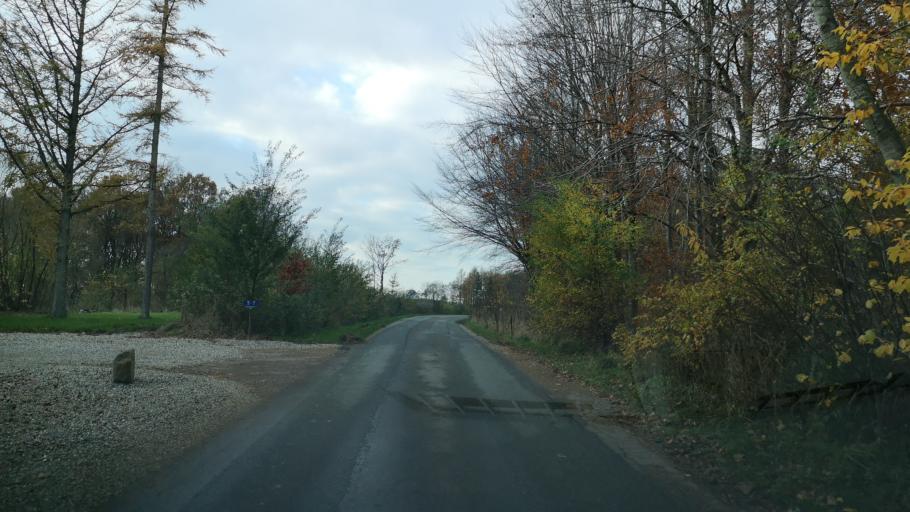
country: DK
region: Central Jutland
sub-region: Ringkobing-Skjern Kommune
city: Videbaek
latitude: 56.0400
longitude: 8.5993
